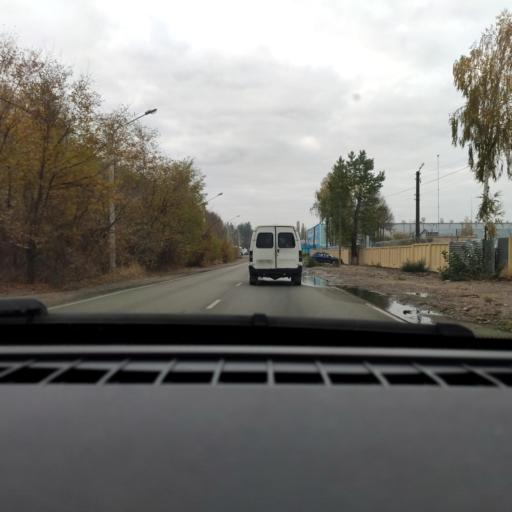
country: RU
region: Voronezj
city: Somovo
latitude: 51.7220
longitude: 39.2953
